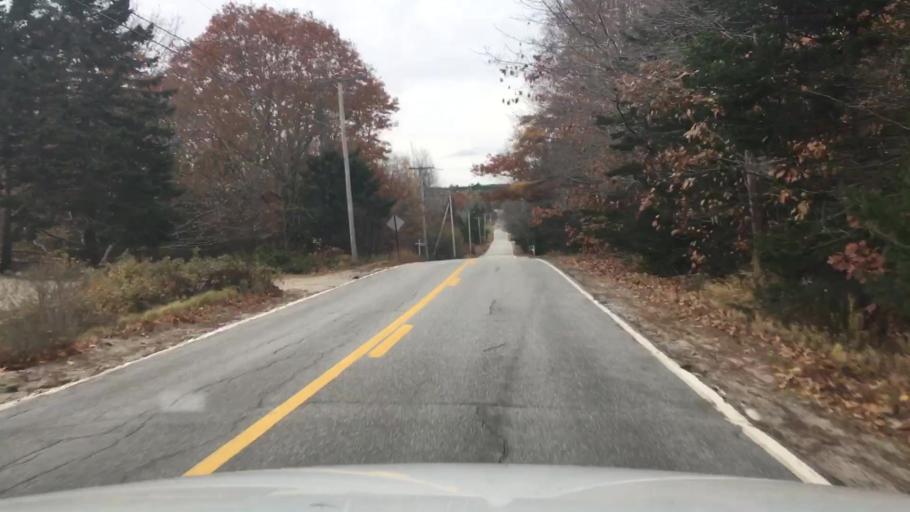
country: US
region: Maine
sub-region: Hancock County
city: Sedgwick
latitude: 44.3323
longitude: -68.5676
